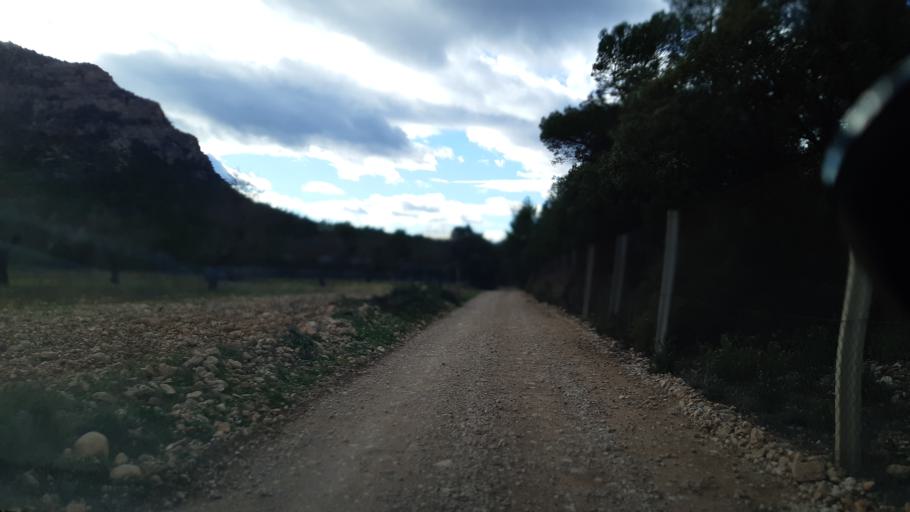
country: ES
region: Aragon
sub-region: Provincia de Teruel
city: Valderrobres
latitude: 40.8531
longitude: 0.2263
